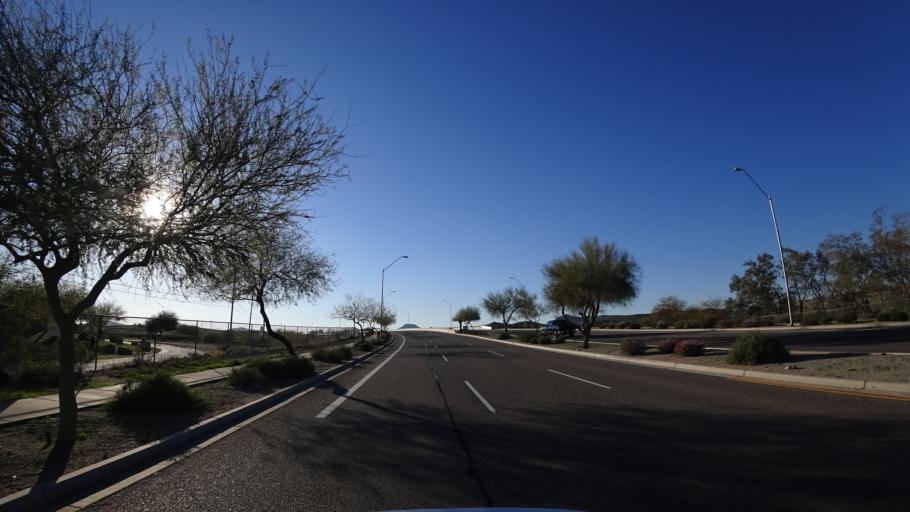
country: US
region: Arizona
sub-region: Maricopa County
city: Anthem
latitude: 33.7131
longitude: -112.1246
